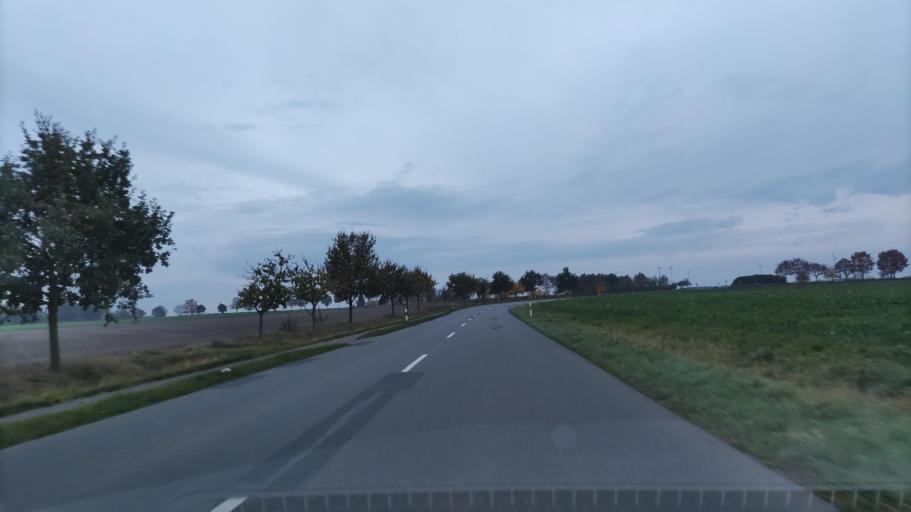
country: DE
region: Lower Saxony
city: Tulau
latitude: 52.6451
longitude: 10.8730
